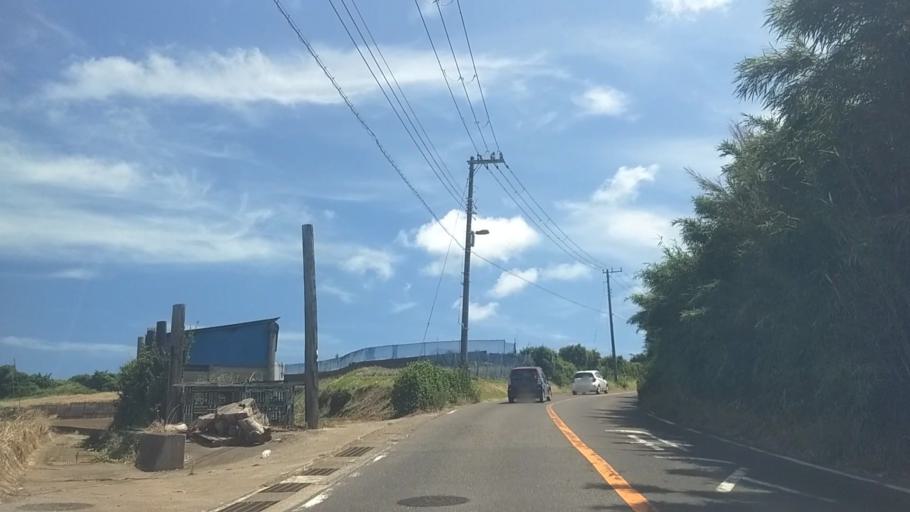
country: JP
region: Kanagawa
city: Miura
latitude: 35.2001
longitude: 139.6509
